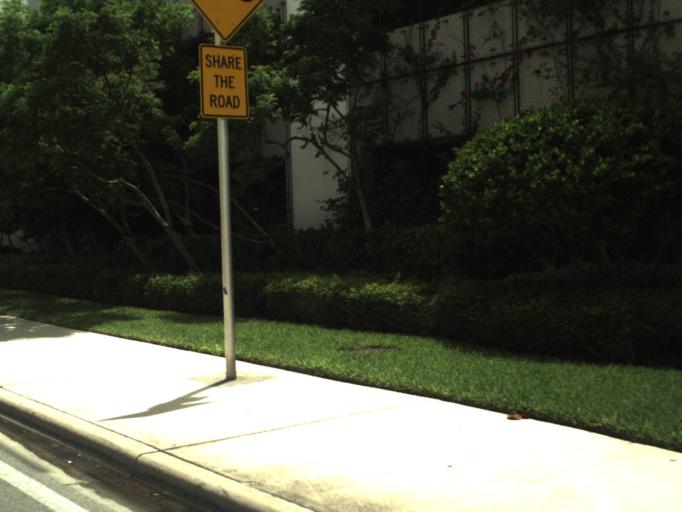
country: US
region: Florida
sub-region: Broward County
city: Hollywood
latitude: 25.9974
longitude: -80.1184
